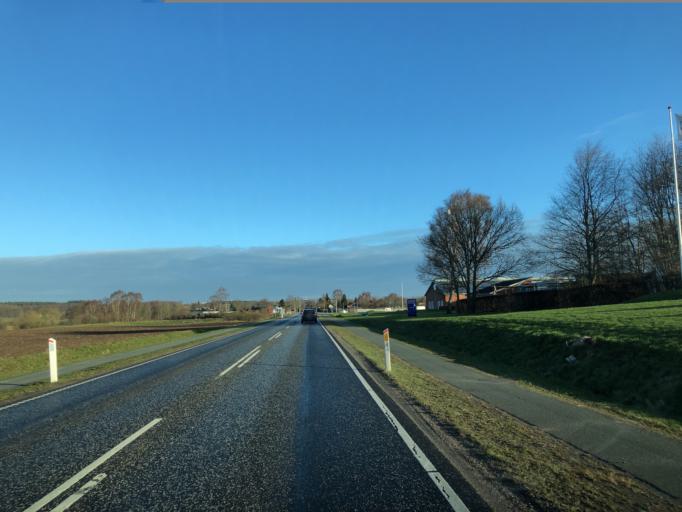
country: DK
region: Central Jutland
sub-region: Favrskov Kommune
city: Hinnerup
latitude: 56.2508
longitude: 10.0698
